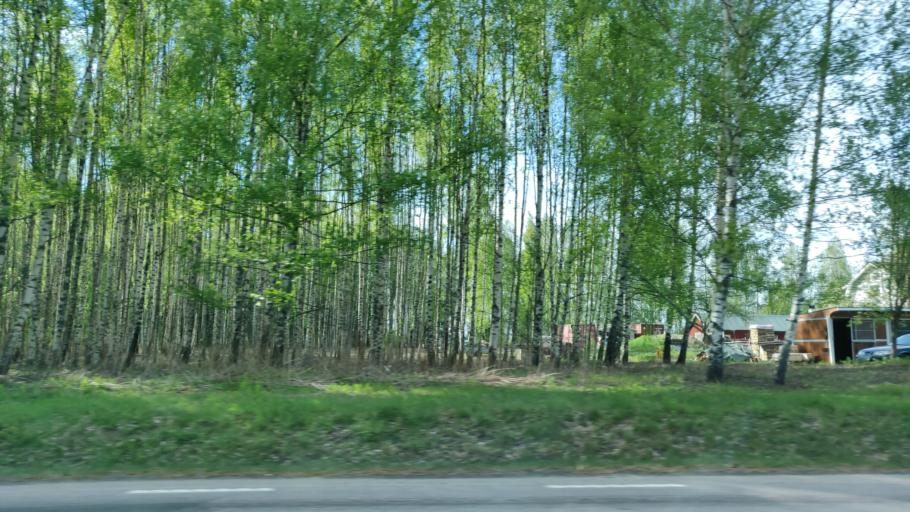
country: SE
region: Vaermland
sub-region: Forshaga Kommun
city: Forshaga
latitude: 59.4945
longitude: 13.4282
